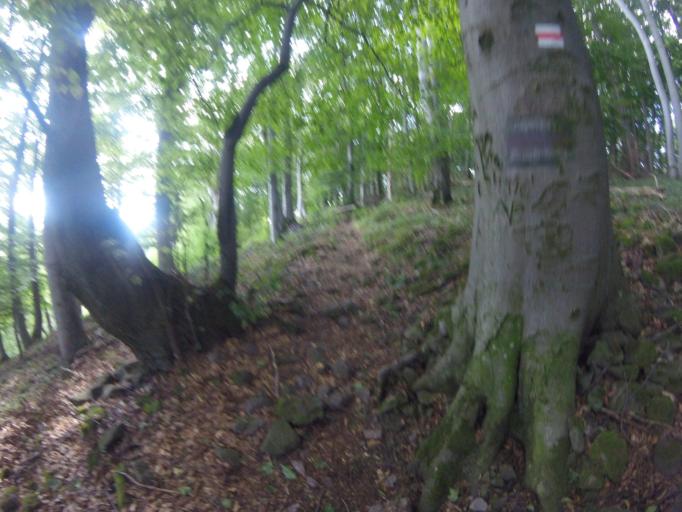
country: SK
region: Nitriansky
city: Sahy
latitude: 47.9761
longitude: 18.8861
